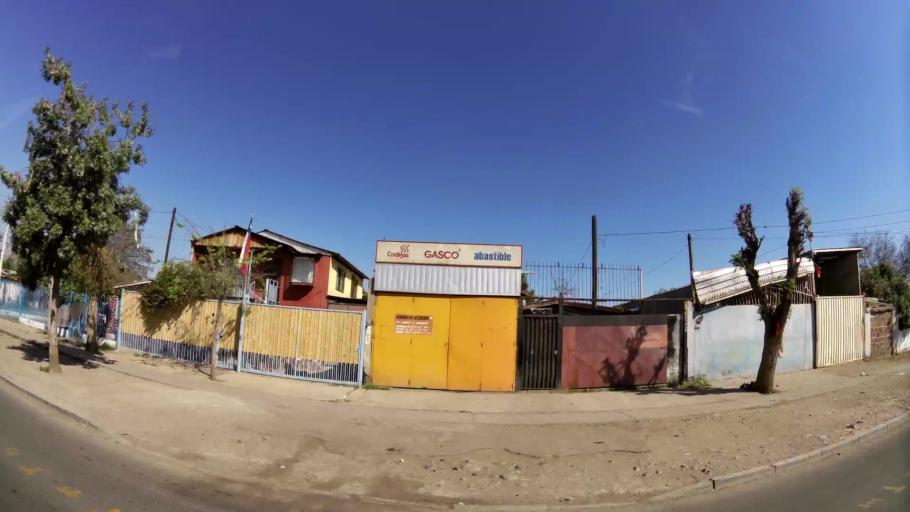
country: CL
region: Santiago Metropolitan
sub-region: Provincia de Santiago
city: La Pintana
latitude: -33.5376
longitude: -70.6117
